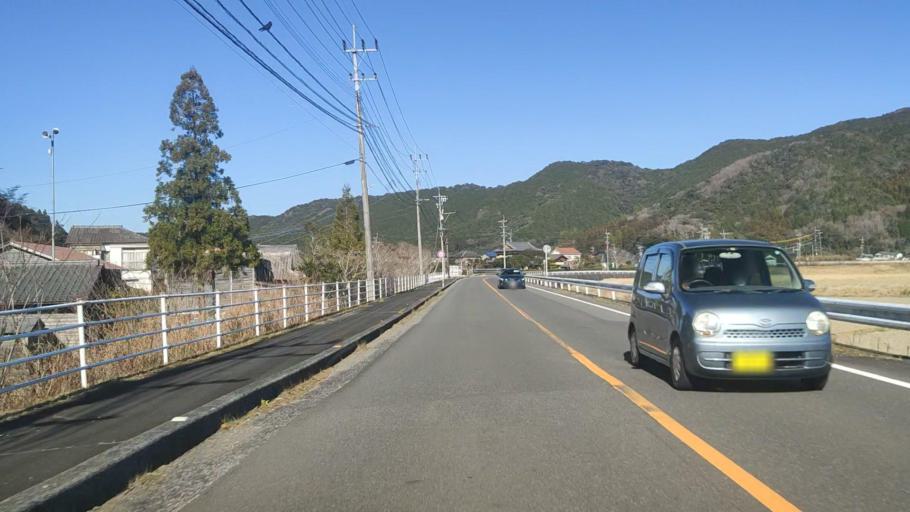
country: JP
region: Oita
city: Saiki
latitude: 32.9289
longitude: 131.9216
